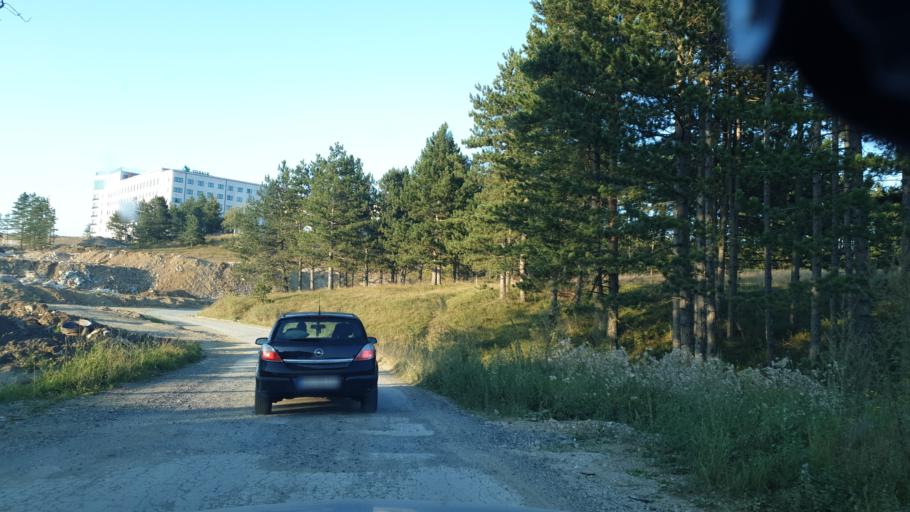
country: RS
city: Zlatibor
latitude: 43.7174
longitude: 19.6935
